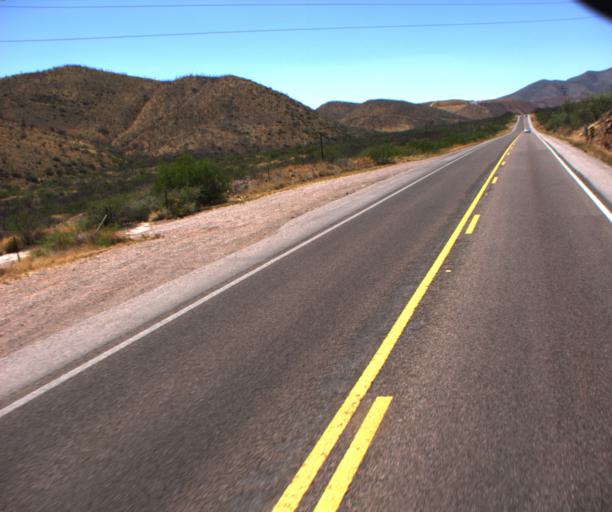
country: US
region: Arizona
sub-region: Cochise County
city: Bisbee
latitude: 31.4331
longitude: -109.8448
